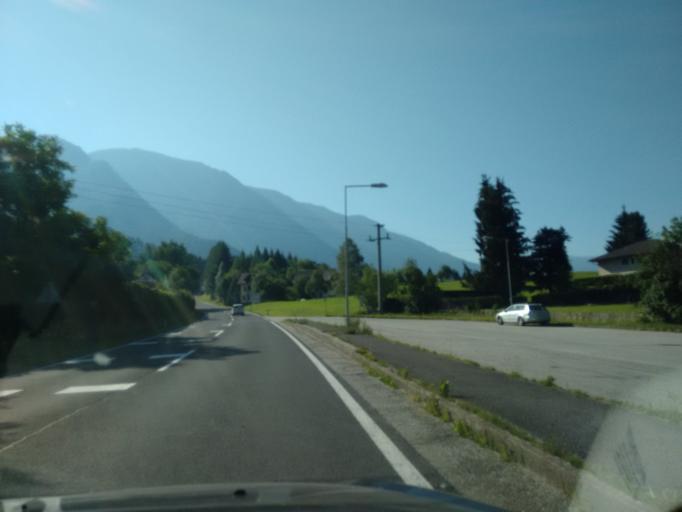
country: AT
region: Upper Austria
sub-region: Politischer Bezirk Gmunden
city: Bad Goisern
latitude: 47.6215
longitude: 13.6479
